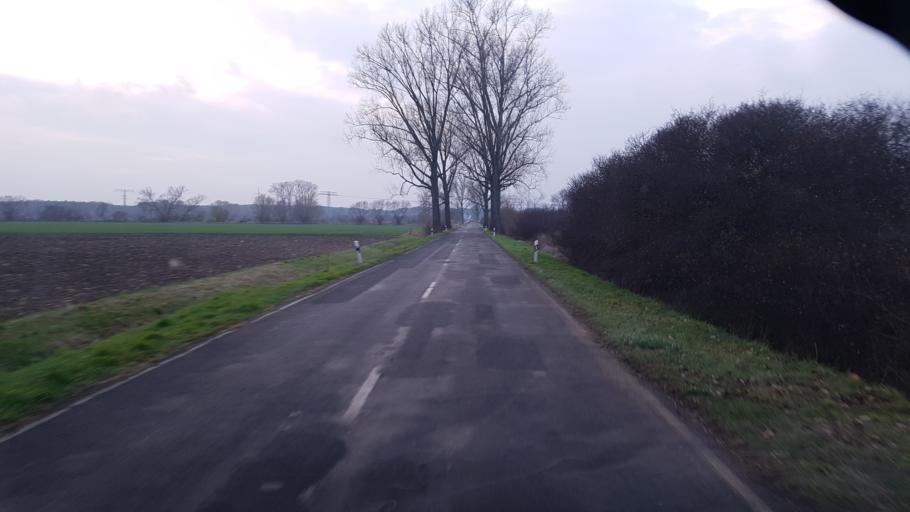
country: DE
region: Brandenburg
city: Ziltendorf
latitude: 52.2125
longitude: 14.6415
